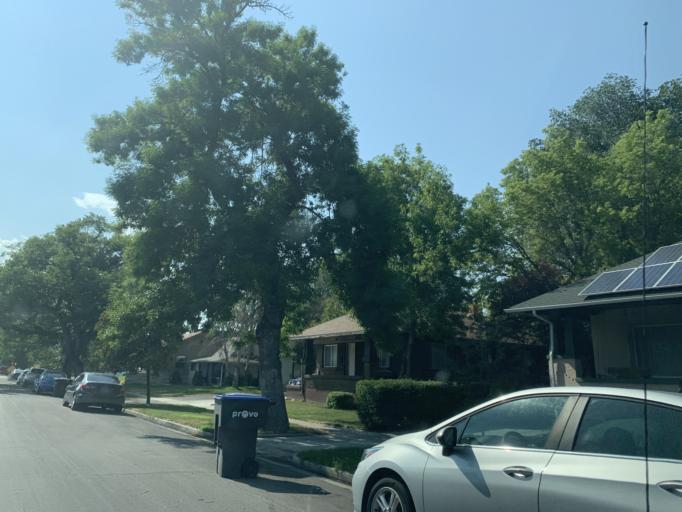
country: US
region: Utah
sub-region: Utah County
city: Provo
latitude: 40.2378
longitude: -111.6644
